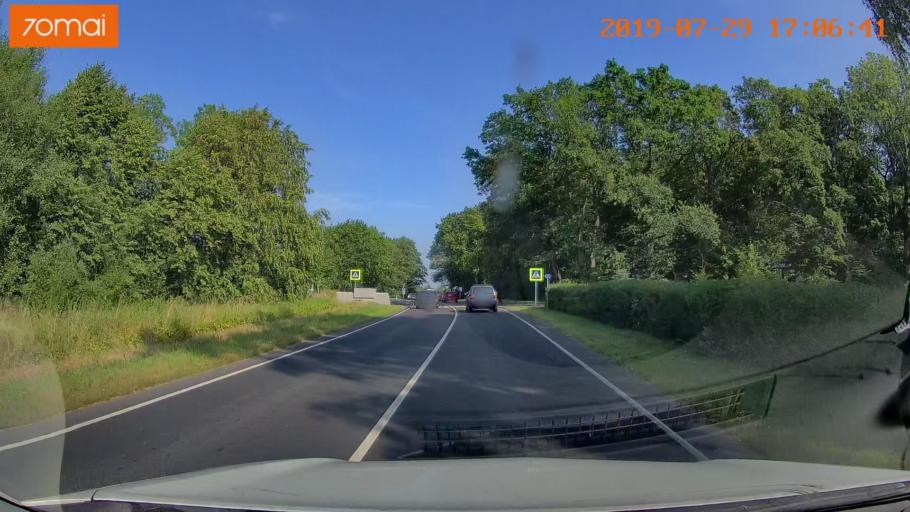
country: RU
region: Kaliningrad
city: Vzmorye
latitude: 54.8193
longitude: 20.3116
